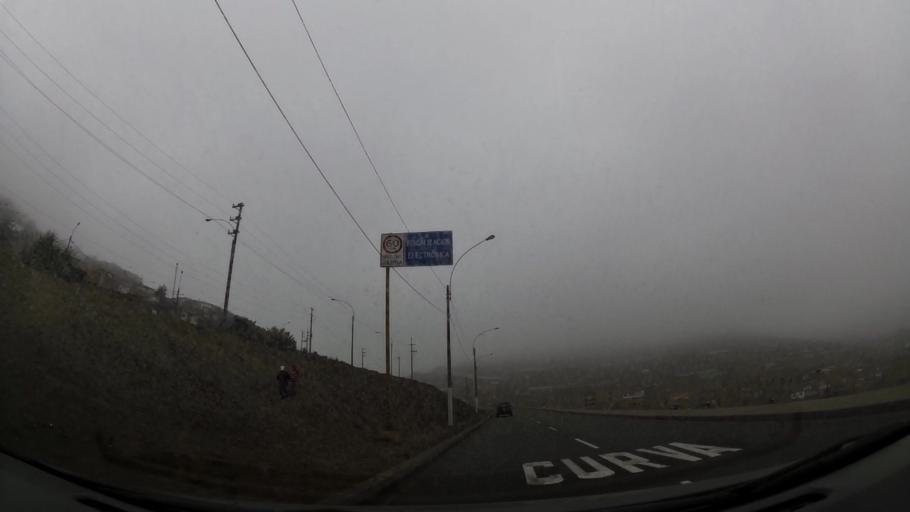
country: PE
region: Lima
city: Ventanilla
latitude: -11.8491
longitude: -77.1213
